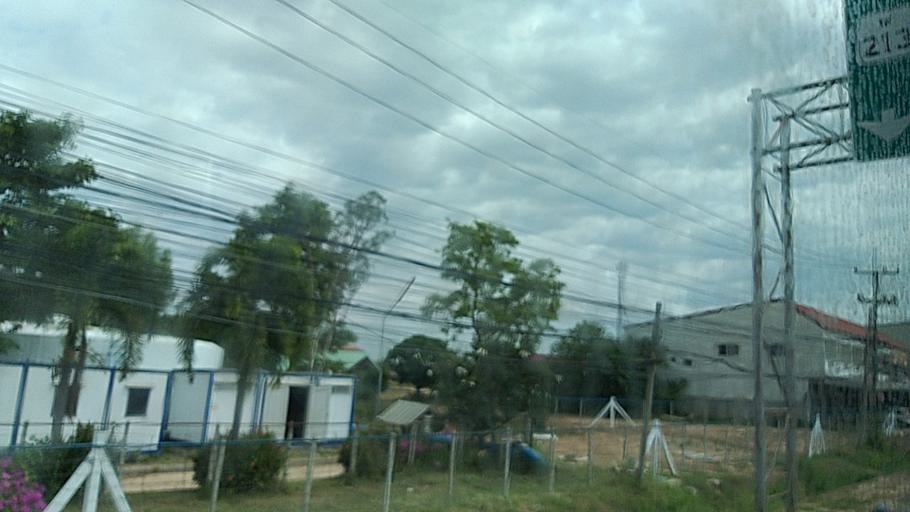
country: TH
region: Maha Sarakham
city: Maha Sarakham
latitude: 16.2163
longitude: 103.2777
